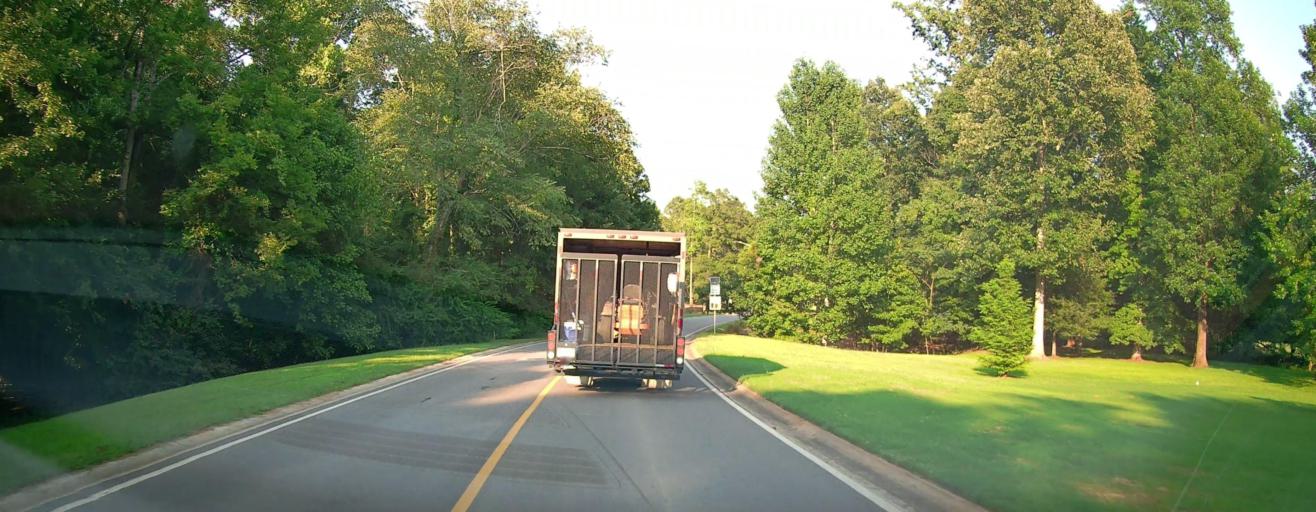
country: US
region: Georgia
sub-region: Bibb County
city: West Point
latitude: 32.8879
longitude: -83.8130
